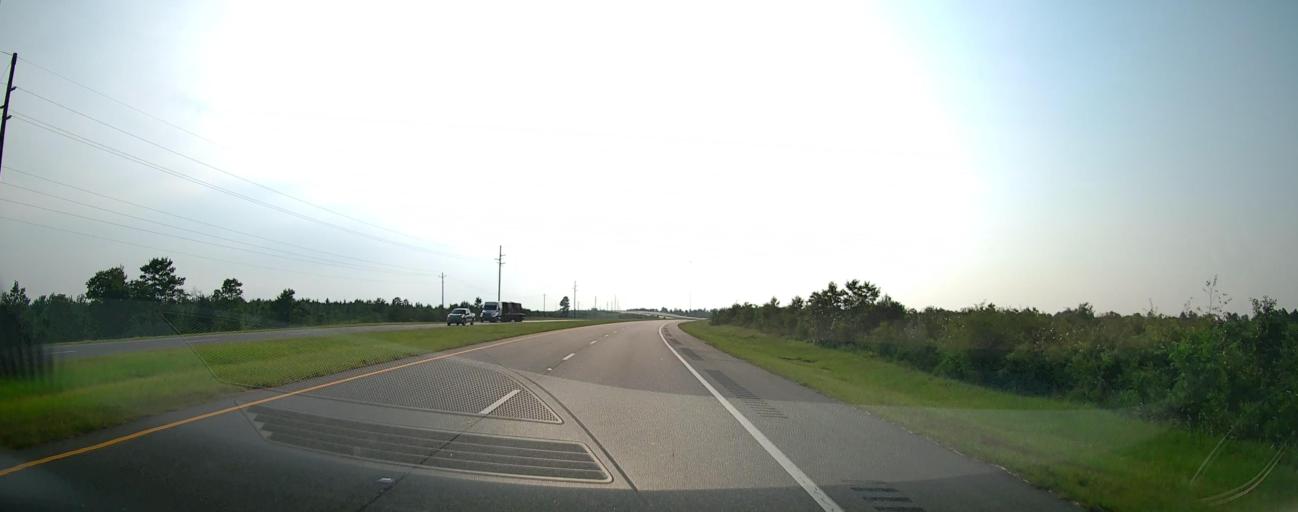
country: US
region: Georgia
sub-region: Talbot County
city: Talbotton
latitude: 32.5950
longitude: -84.4394
